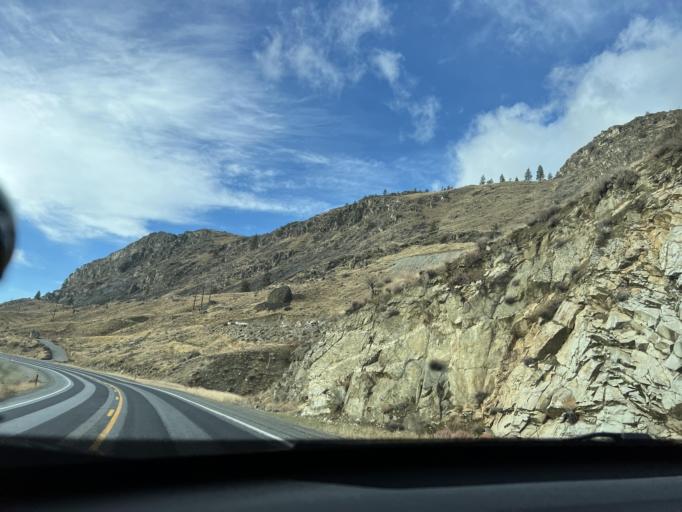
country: US
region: Washington
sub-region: Chelan County
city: Chelan
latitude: 47.8537
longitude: -119.9639
